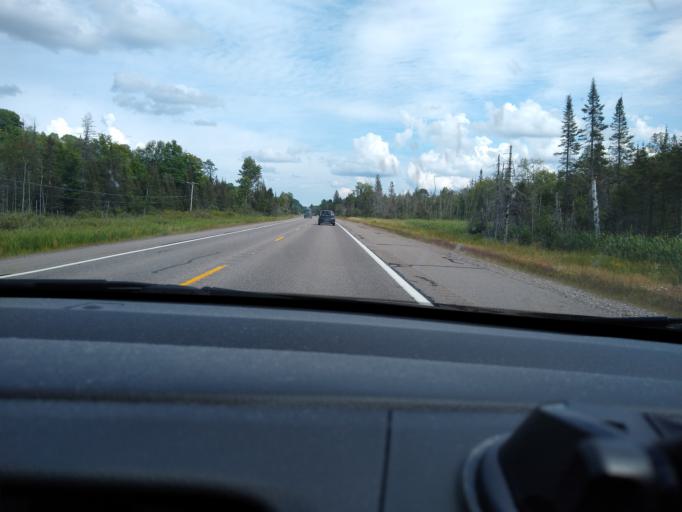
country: US
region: Michigan
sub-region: Marquette County
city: West Ishpeming
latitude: 46.5427
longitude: -88.0679
